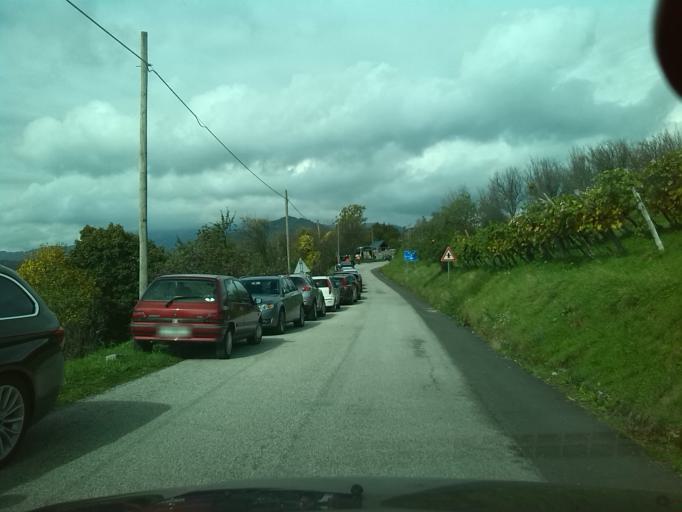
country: IT
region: Friuli Venezia Giulia
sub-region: Provincia di Udine
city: Clodig
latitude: 46.1422
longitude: 13.6159
